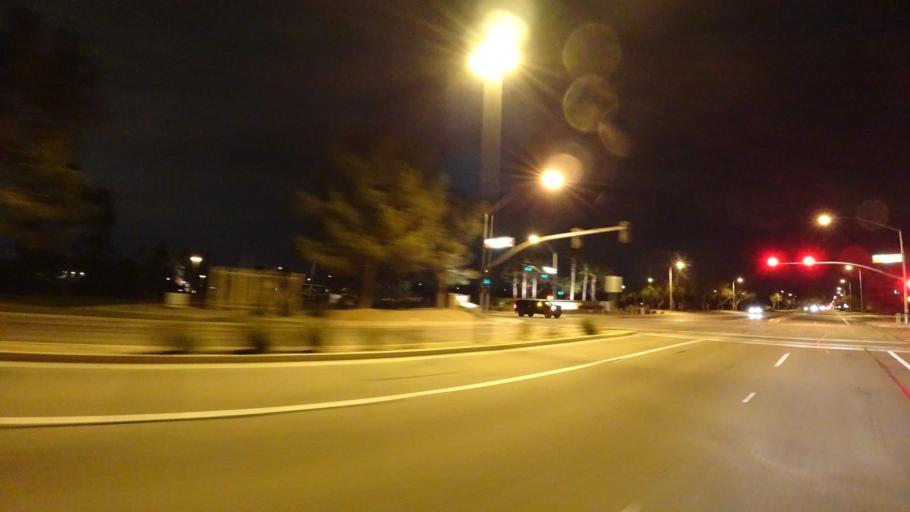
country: US
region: Arizona
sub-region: Maricopa County
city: Sun Lakes
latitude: 33.2473
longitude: -111.8589
